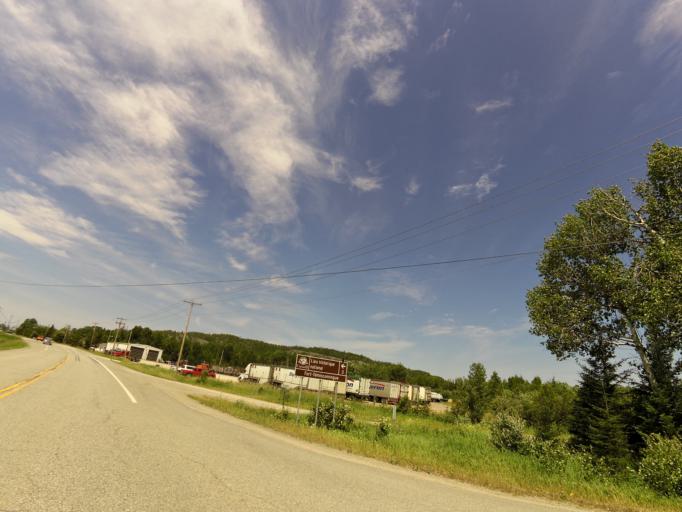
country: CA
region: Quebec
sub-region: Abitibi-Temiscamingue
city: Ville-Marie
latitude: 47.2942
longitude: -79.4221
